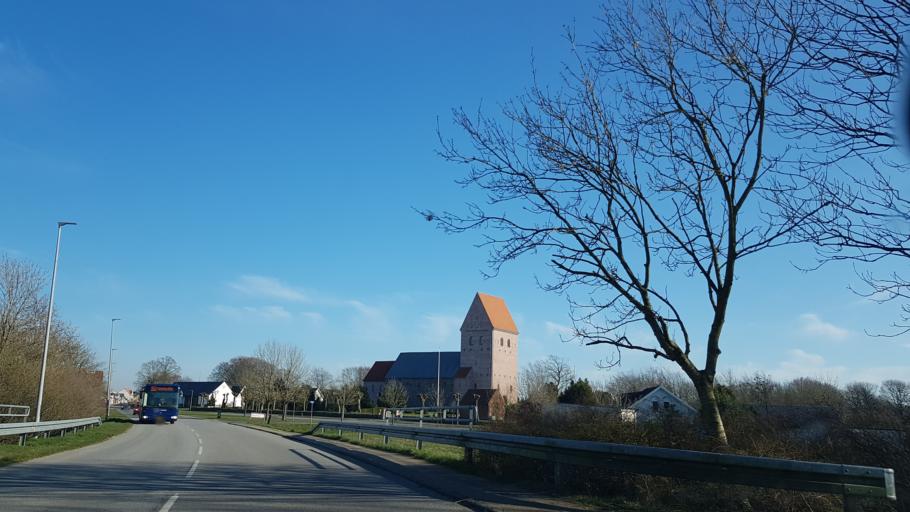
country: DK
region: South Denmark
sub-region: Kolding Kommune
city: Vamdrup
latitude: 55.4295
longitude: 9.2710
